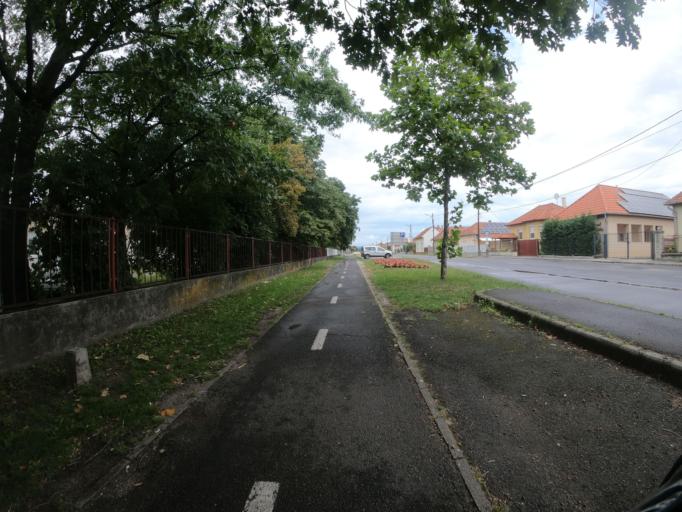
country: HU
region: Borsod-Abauj-Zemplen
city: Mezokovesd
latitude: 47.8009
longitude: 20.5692
